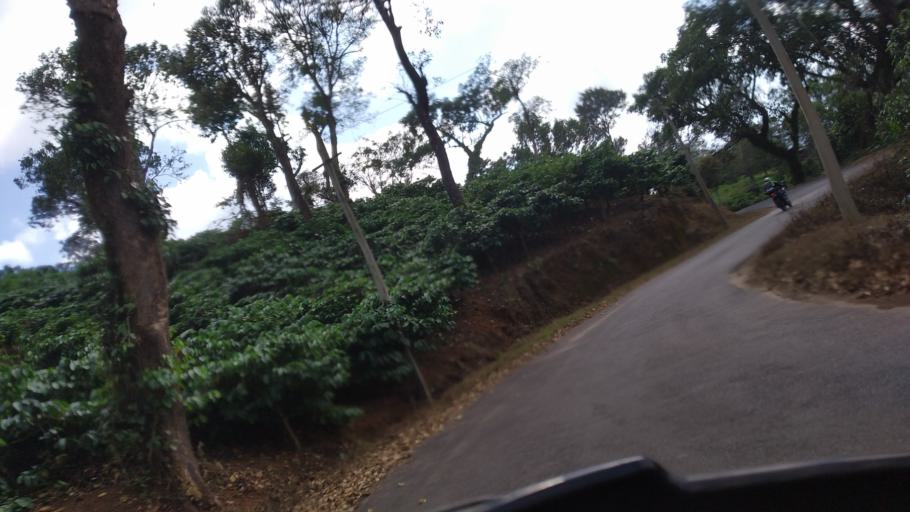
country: IN
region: Karnataka
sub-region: Kodagu
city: Ponnampet
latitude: 12.0319
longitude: 75.9209
